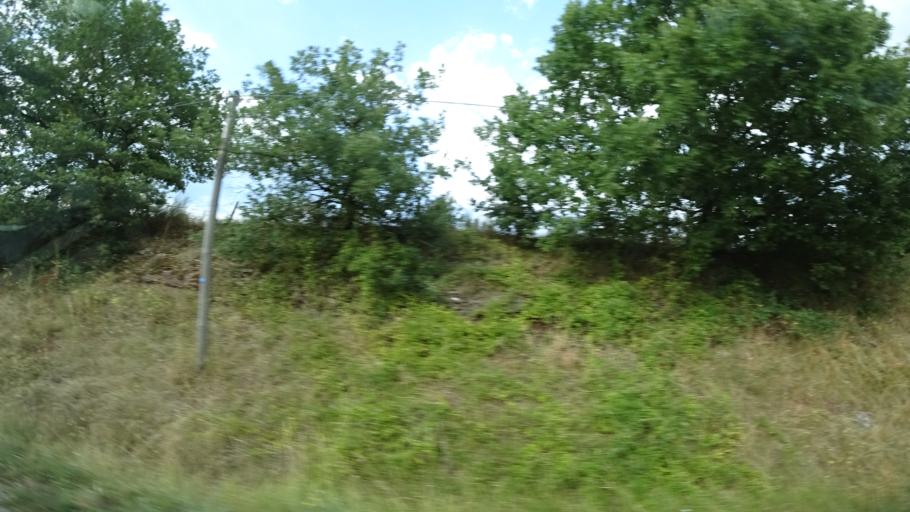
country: FR
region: Midi-Pyrenees
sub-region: Departement de l'Aveyron
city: Saint-Christophe-Vallon
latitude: 44.5052
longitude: 2.3670
